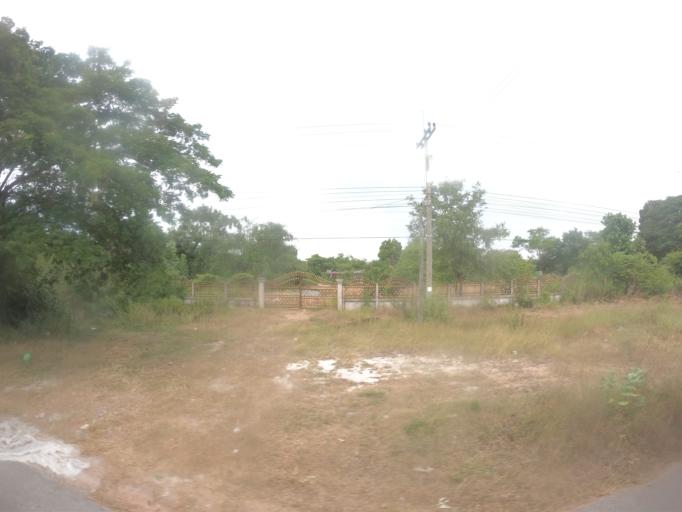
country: TH
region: Maha Sarakham
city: Kantharawichai
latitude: 16.3396
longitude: 103.2017
